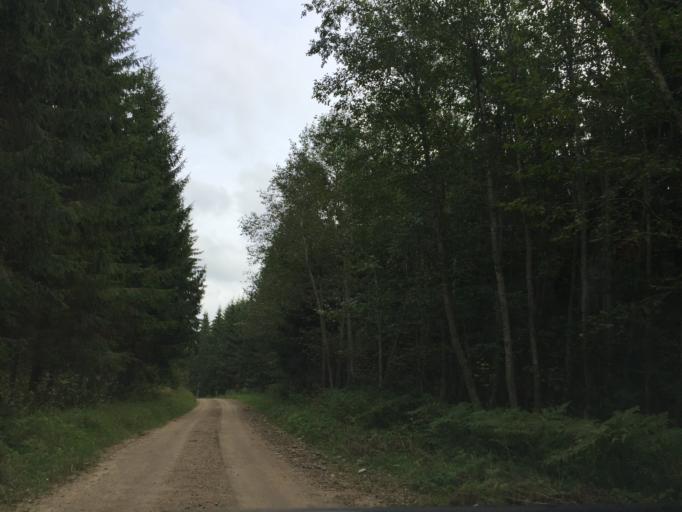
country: LV
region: Dagda
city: Dagda
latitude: 56.2115
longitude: 27.8186
